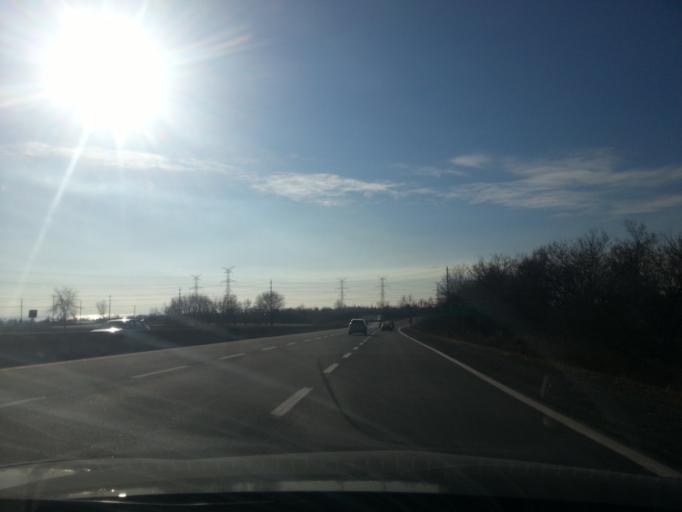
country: CA
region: Ontario
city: Oshawa
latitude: 43.9062
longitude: -78.6221
